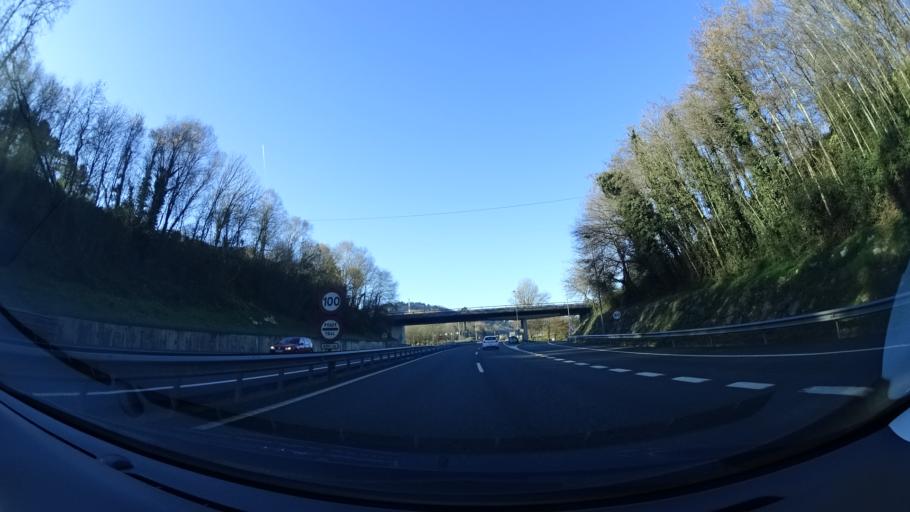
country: ES
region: Basque Country
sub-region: Provincia de Guipuzcoa
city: Irun
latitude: 43.3195
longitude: -1.8292
